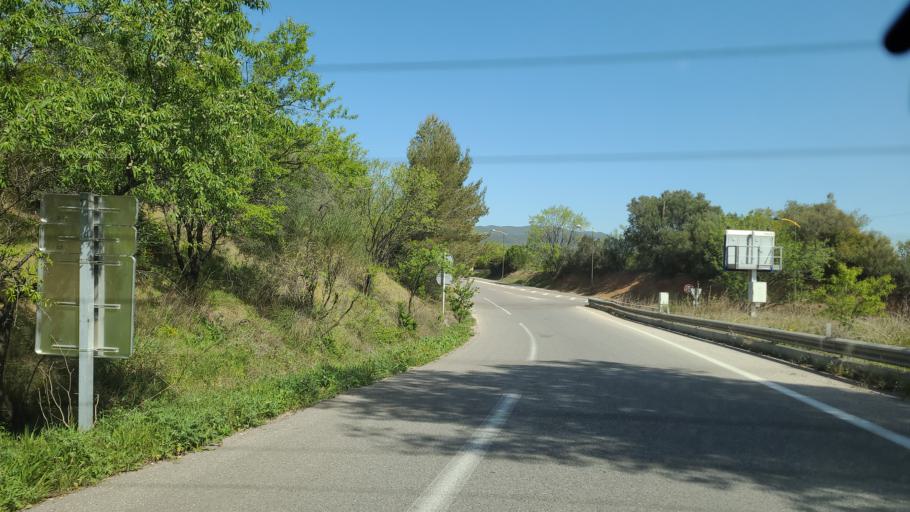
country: FR
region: Provence-Alpes-Cote d'Azur
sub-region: Departement du Var
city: Cuers
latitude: 43.2234
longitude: 6.0701
